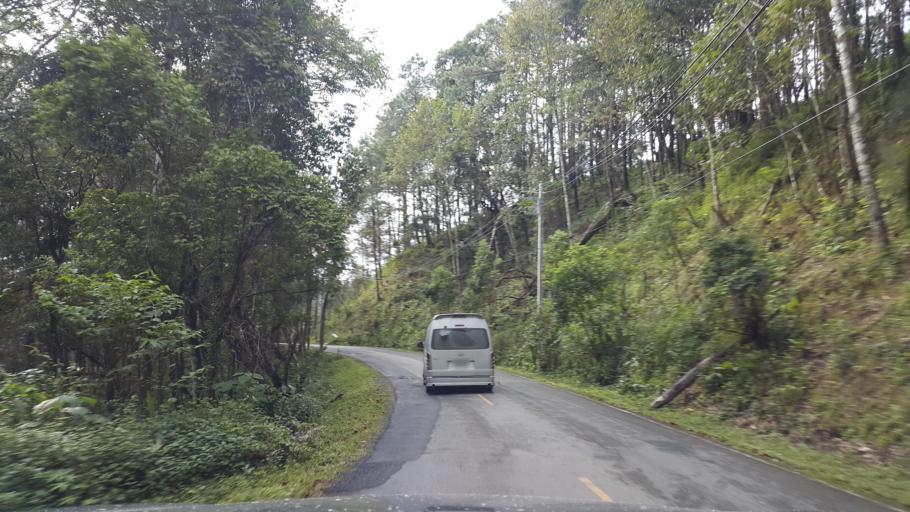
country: TH
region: Chiang Mai
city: Chaem Luang
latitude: 18.9294
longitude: 98.4796
